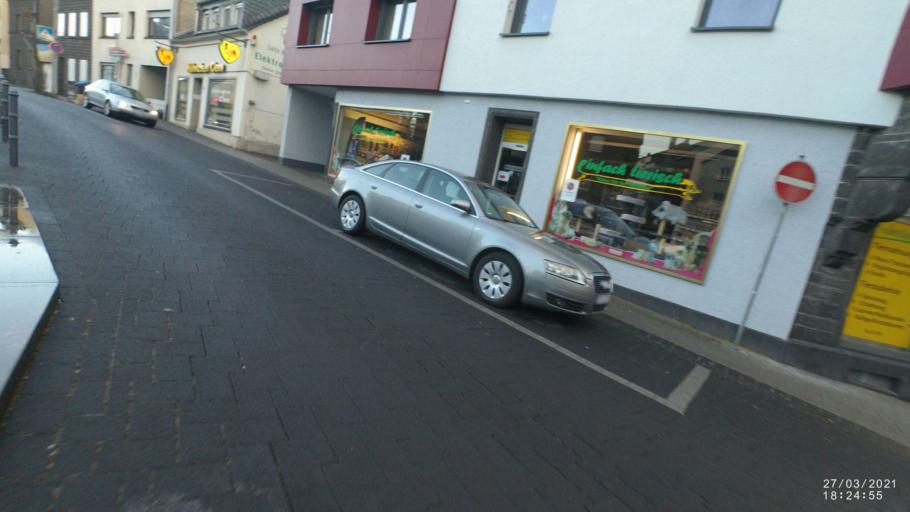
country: DE
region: Rheinland-Pfalz
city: Mendig
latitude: 50.3729
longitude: 7.2801
